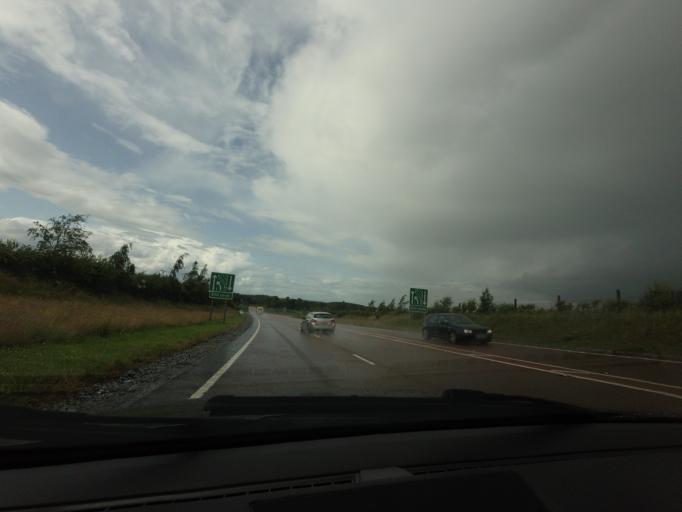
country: GB
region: Scotland
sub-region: Moray
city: Fochabers
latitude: 57.6131
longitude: -3.0874
